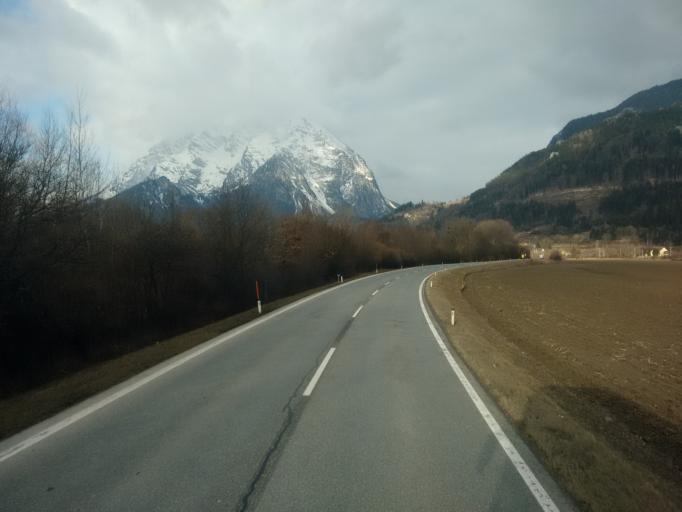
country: AT
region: Styria
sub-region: Politischer Bezirk Liezen
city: Stainach
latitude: 47.5249
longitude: 14.1028
